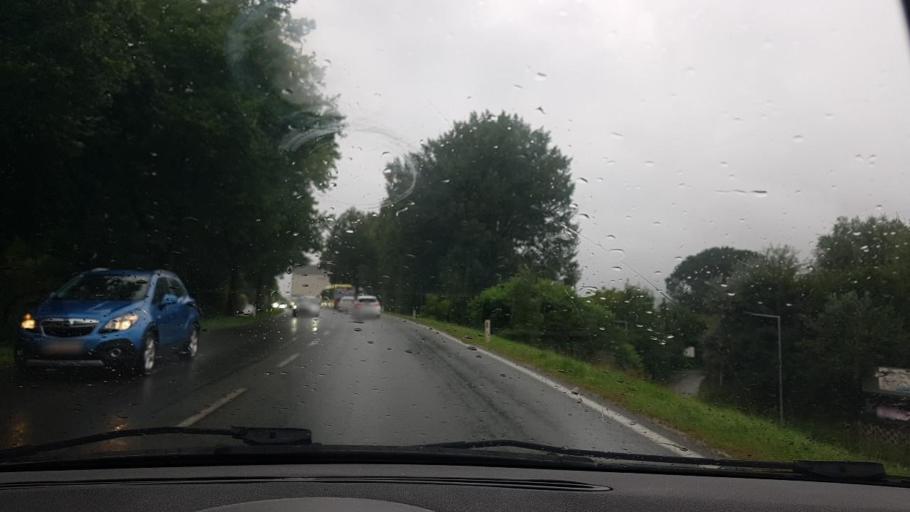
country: AT
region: Tyrol
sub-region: Politischer Bezirk Innsbruck Land
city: Absam
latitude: 47.2770
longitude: 11.4848
